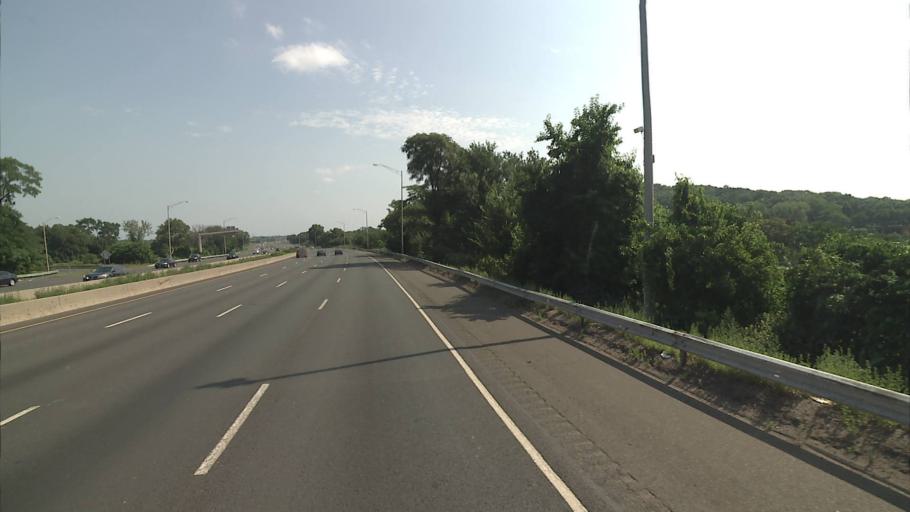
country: US
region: Connecticut
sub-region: New Haven County
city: New Haven
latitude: 41.3245
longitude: -72.8823
